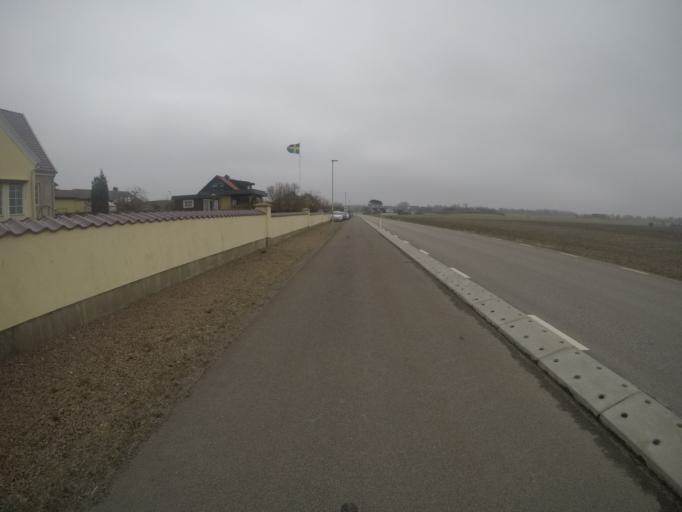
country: SE
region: Skane
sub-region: Angelholms Kommun
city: Strovelstorp
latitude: 56.2157
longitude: 12.7797
